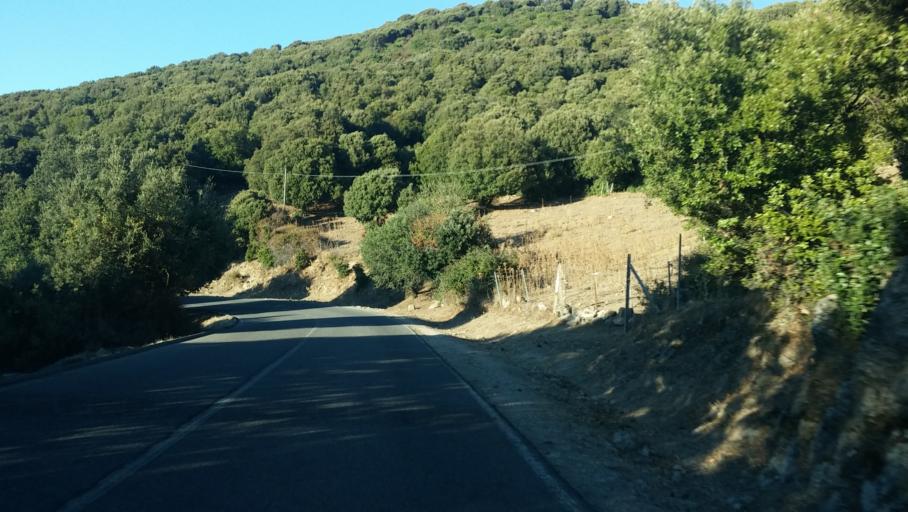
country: IT
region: Sardinia
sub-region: Provincia di Nuoro
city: Orgosolo
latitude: 40.1925
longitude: 9.3552
